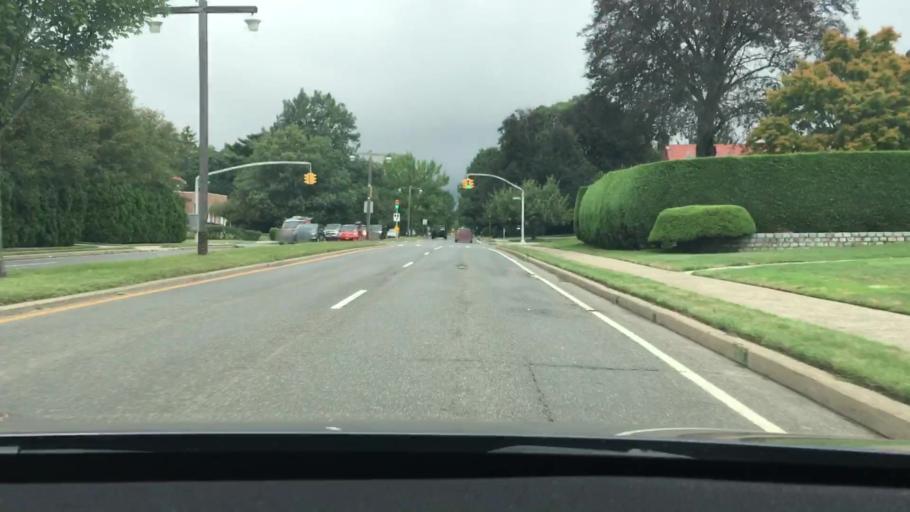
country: US
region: New York
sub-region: Nassau County
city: Garden City Park
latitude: 40.7289
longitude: -73.6607
